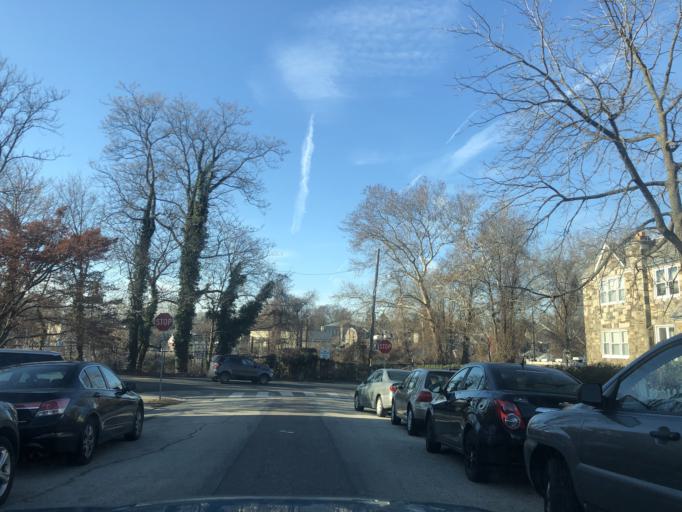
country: US
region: Pennsylvania
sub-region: Delaware County
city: Millbourne
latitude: 39.9860
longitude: -75.2444
